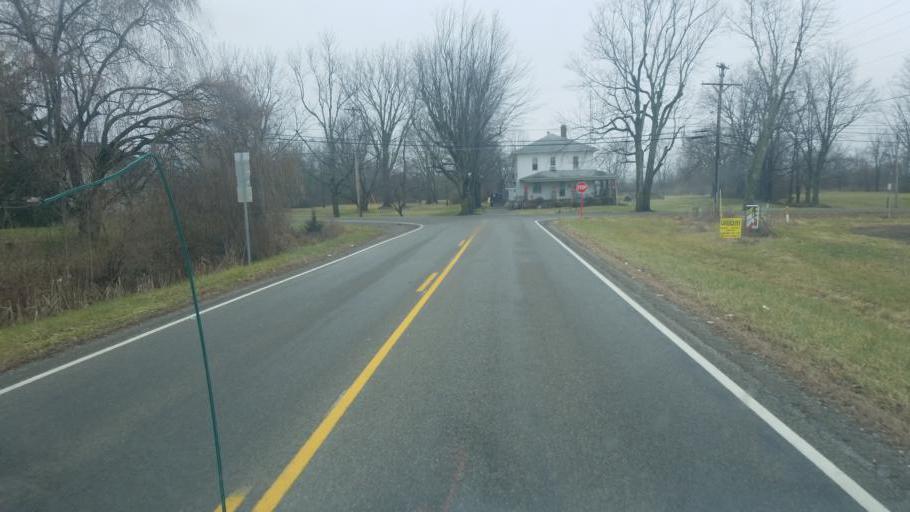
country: US
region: Ohio
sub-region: Champaign County
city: North Lewisburg
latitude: 40.3330
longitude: -83.5766
